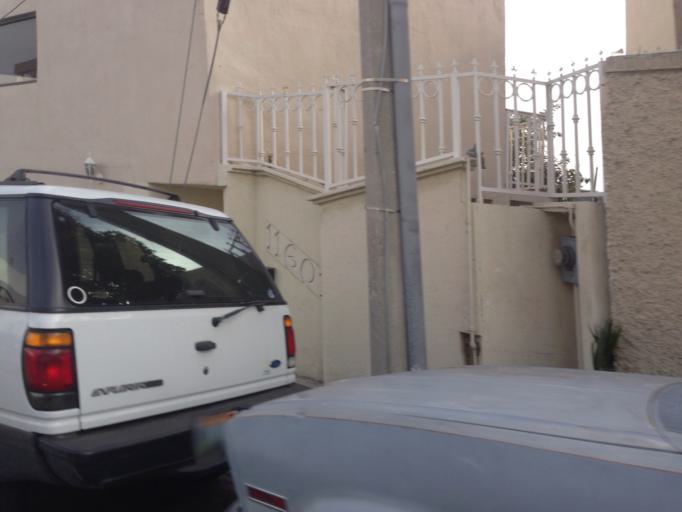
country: MX
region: Baja California
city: Tijuana
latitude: 32.4965
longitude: -117.0015
